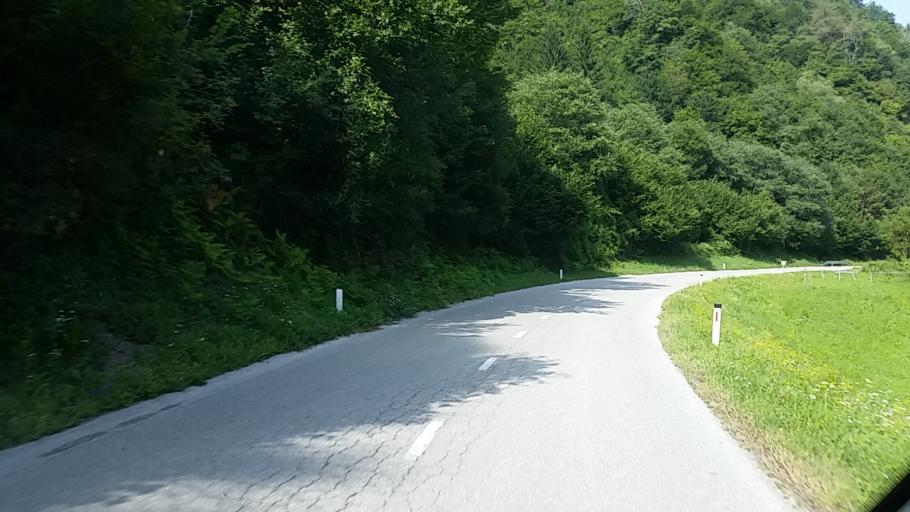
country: SI
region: Zelezniki
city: Zelezniki
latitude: 46.2096
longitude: 14.0511
